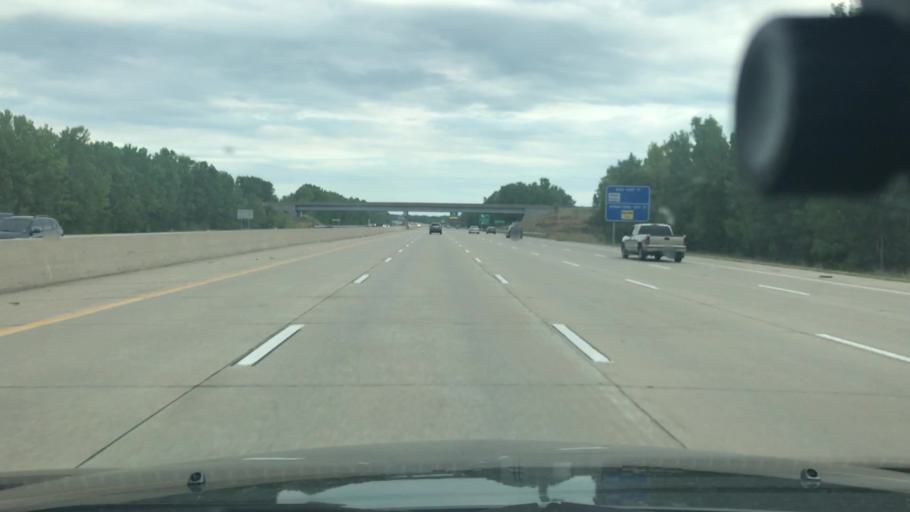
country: US
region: Missouri
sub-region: Saint Charles County
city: Saint Charles
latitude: 38.7214
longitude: -90.5118
